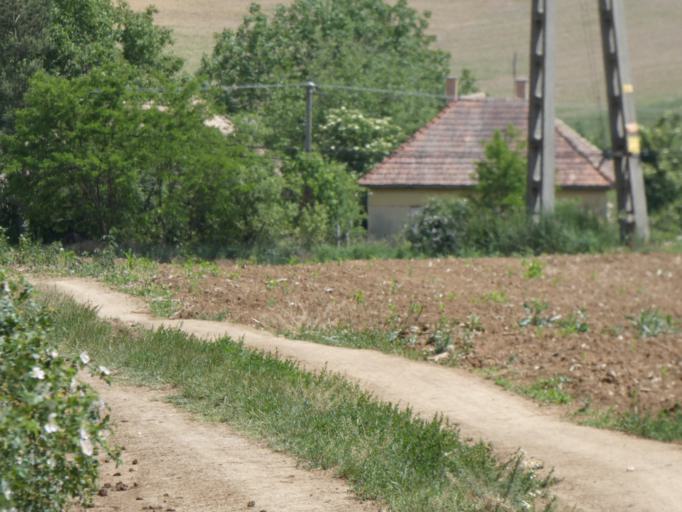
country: HU
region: Nograd
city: Romhany
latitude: 47.8759
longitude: 19.3088
